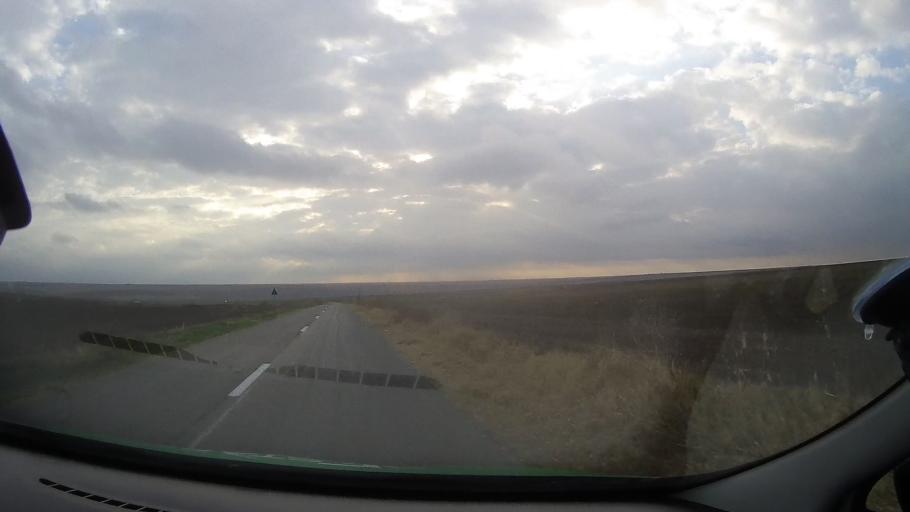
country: RO
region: Constanta
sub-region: Comuna Deleni
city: Pietreni
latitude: 44.1253
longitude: 28.1075
